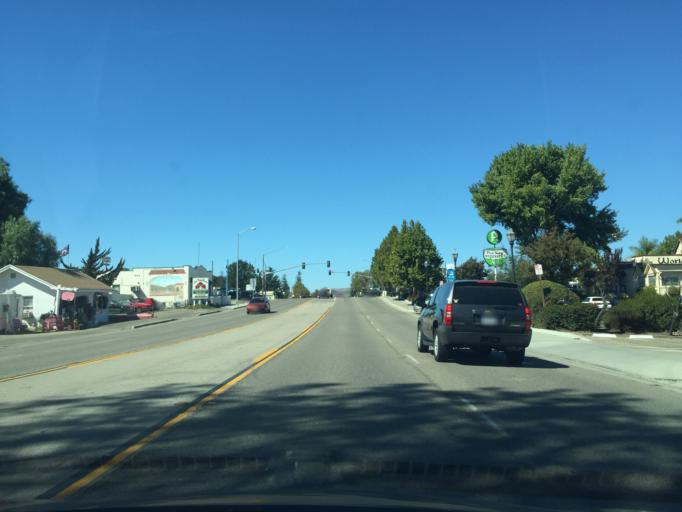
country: US
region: California
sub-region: Santa Barbara County
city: Buellton
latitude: 34.6130
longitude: -120.1922
